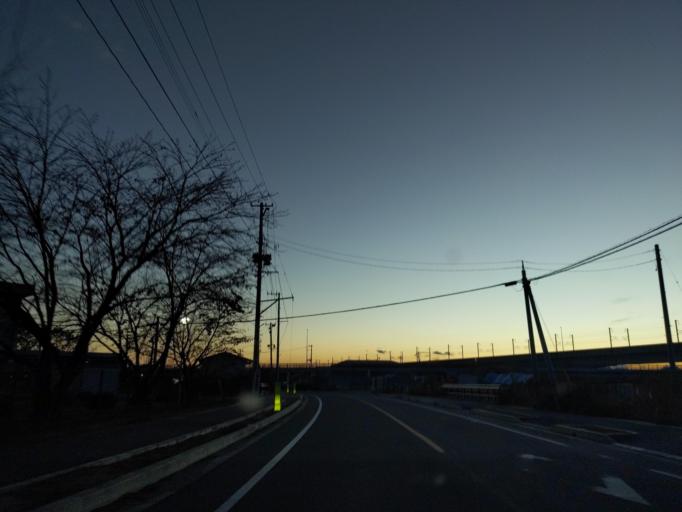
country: JP
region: Fukushima
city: Koriyama
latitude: 37.3592
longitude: 140.3778
